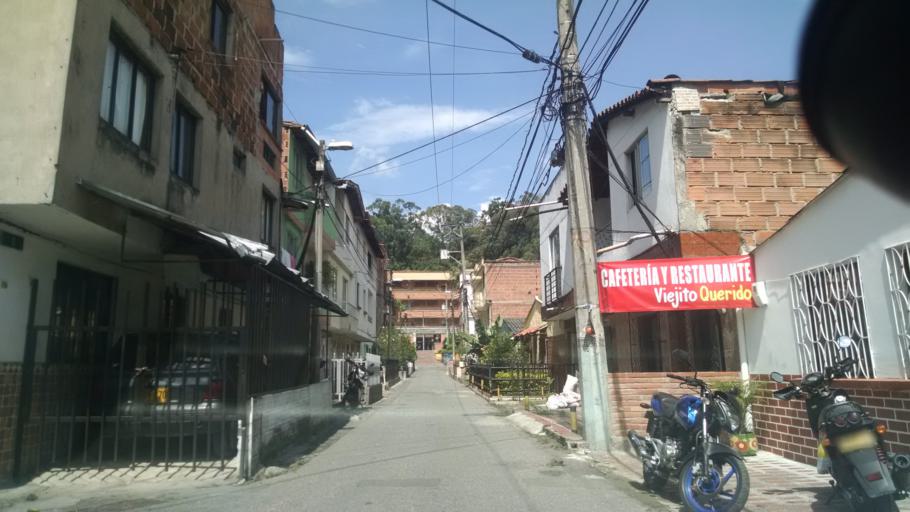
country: CO
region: Antioquia
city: Itagui
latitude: 6.2020
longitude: -75.5890
